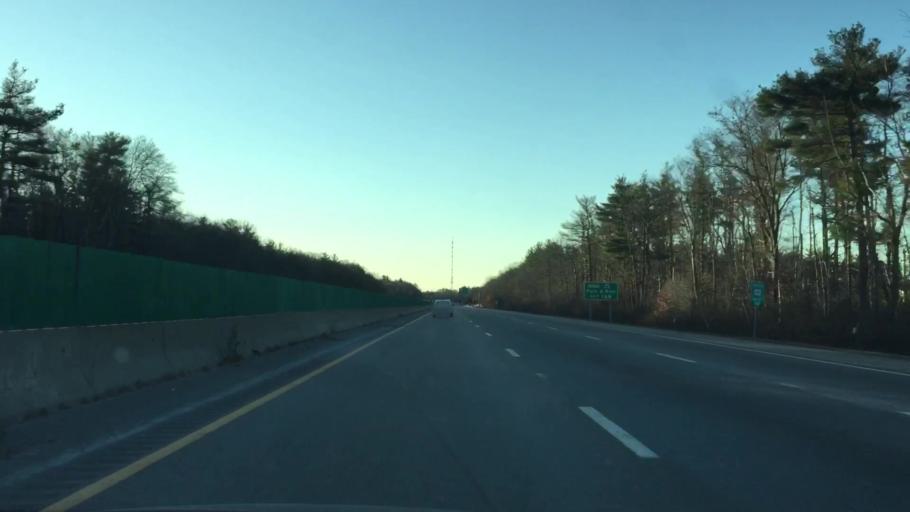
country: US
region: Massachusetts
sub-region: Plymouth County
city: West Bridgewater
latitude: 42.0300
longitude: -71.0509
